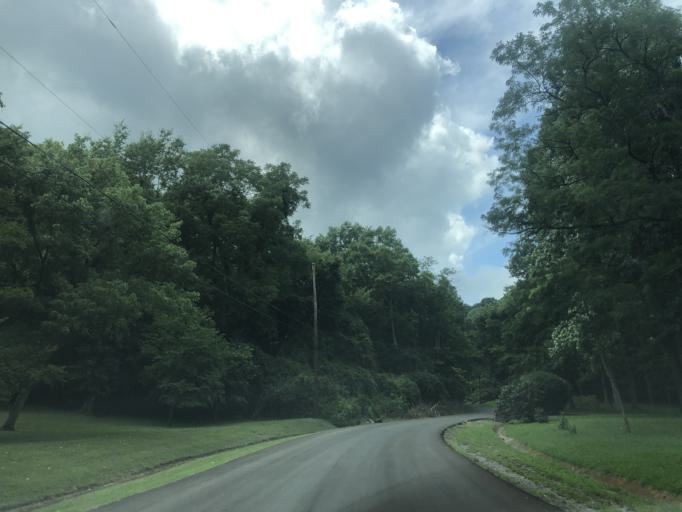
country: US
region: Tennessee
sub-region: Davidson County
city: Forest Hills
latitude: 36.0686
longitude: -86.8142
